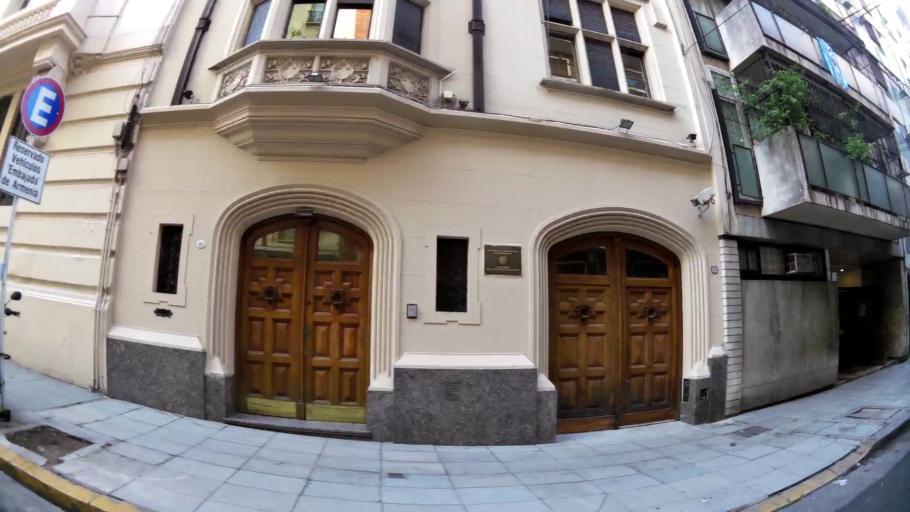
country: AR
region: Buenos Aires F.D.
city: Retiro
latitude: -34.5919
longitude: -58.3945
